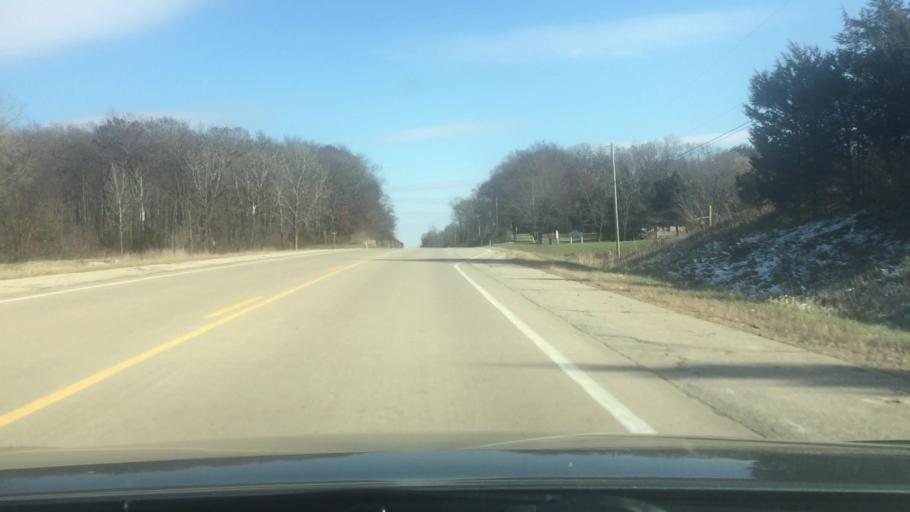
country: US
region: Wisconsin
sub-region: Jefferson County
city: Lake Ripley
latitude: 42.9737
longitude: -88.9349
